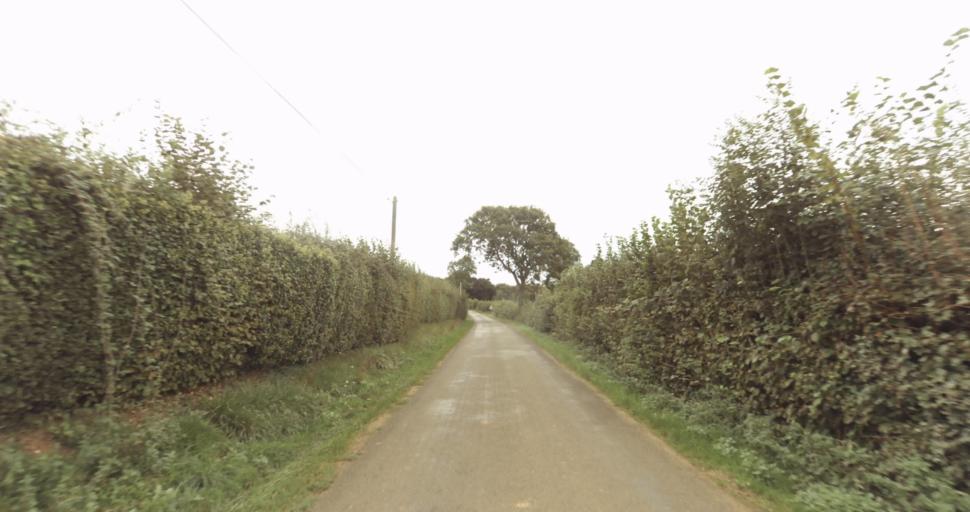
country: FR
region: Lower Normandy
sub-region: Departement de l'Orne
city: Gace
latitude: 48.7227
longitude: 0.3211
